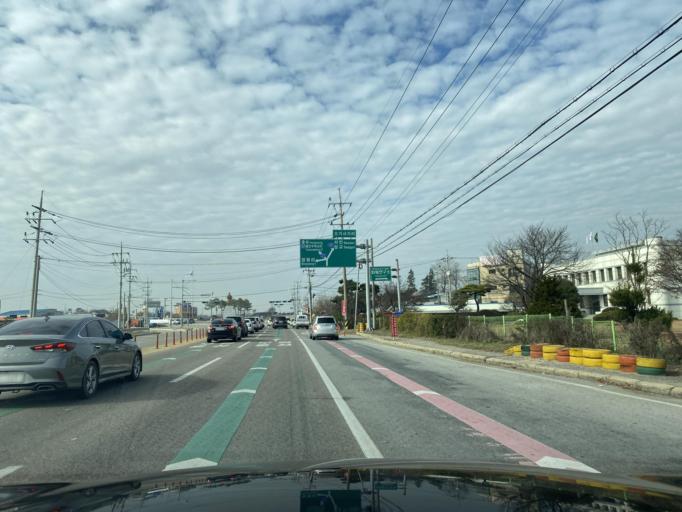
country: KR
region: Chungcheongnam-do
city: Yesan
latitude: 36.6850
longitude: 126.8088
